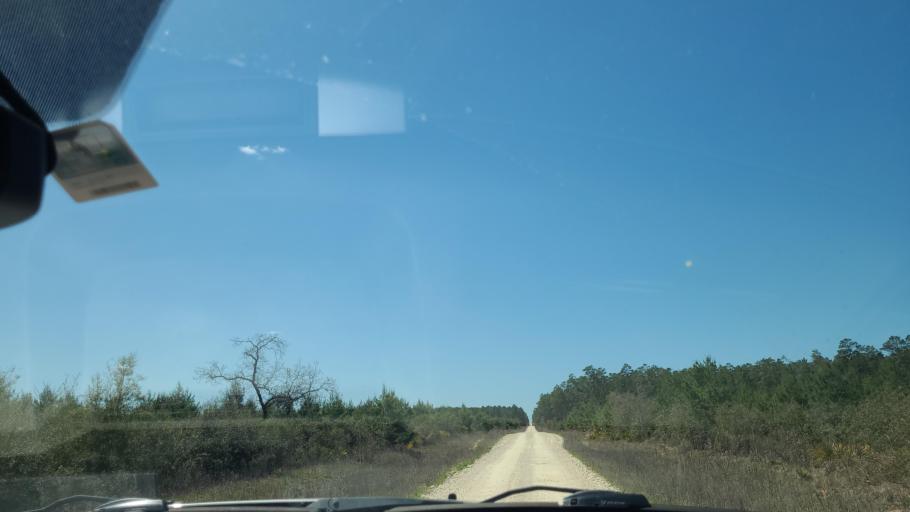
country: US
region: Florida
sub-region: Putnam County
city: Interlachen
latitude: 29.4284
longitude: -81.8666
